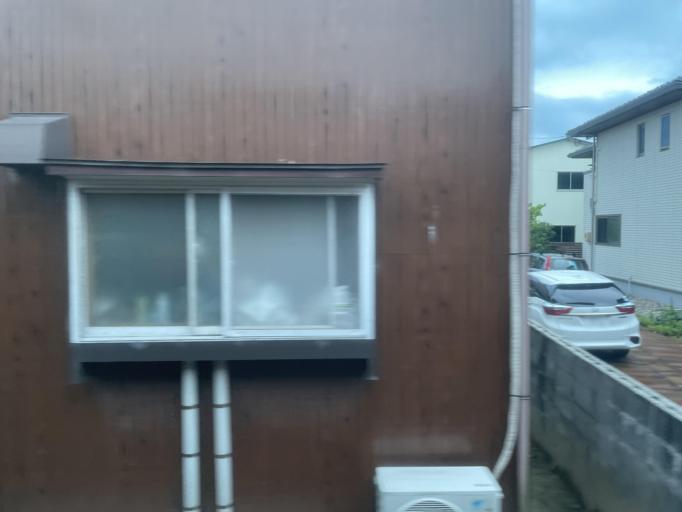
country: JP
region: Niigata
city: Tsubame
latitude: 37.6679
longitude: 138.9246
